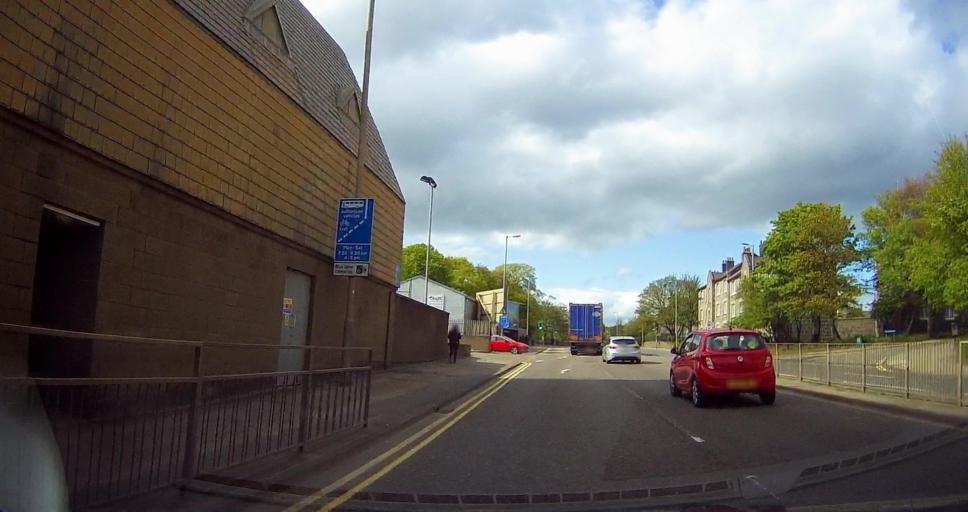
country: GB
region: Scotland
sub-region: Aberdeen City
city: Aberdeen
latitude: 57.1303
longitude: -2.0936
